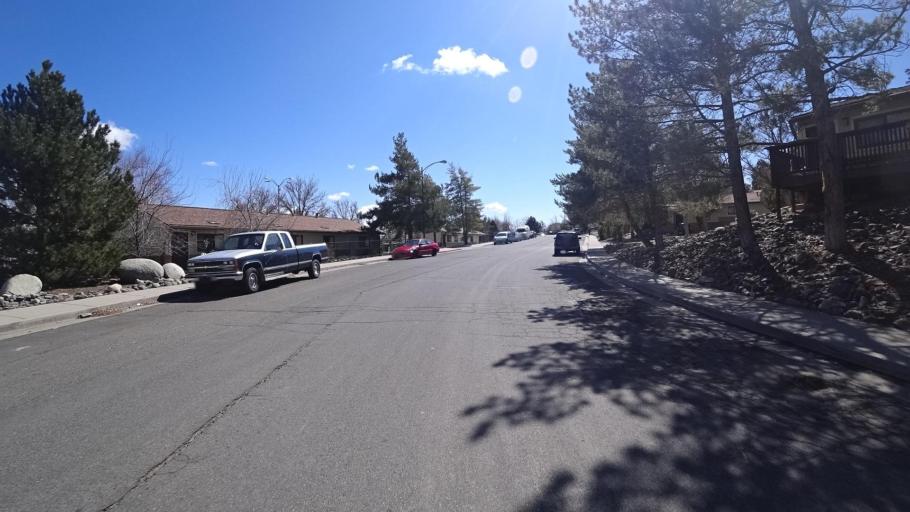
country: US
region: Nevada
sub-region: Washoe County
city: Golden Valley
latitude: 39.5933
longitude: -119.8442
